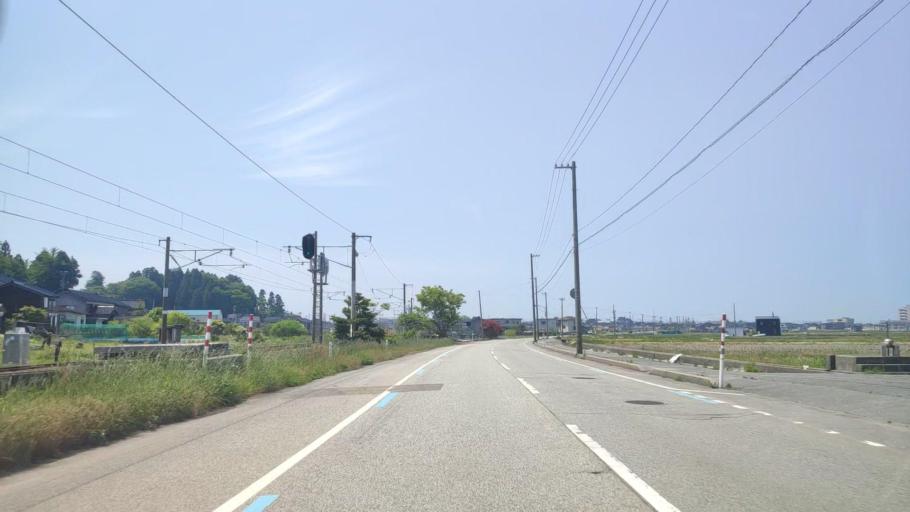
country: JP
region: Toyama
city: Nyuzen
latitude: 36.9628
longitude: 137.5737
